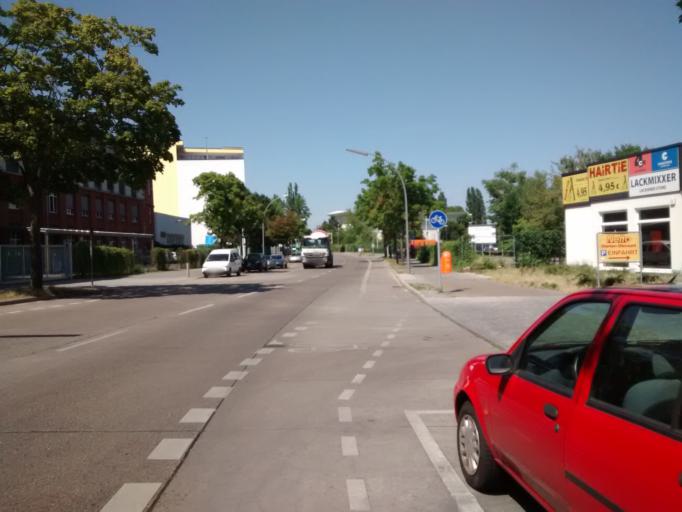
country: DE
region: Berlin
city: Charlottenburg-Nord
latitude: 52.5267
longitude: 13.3063
